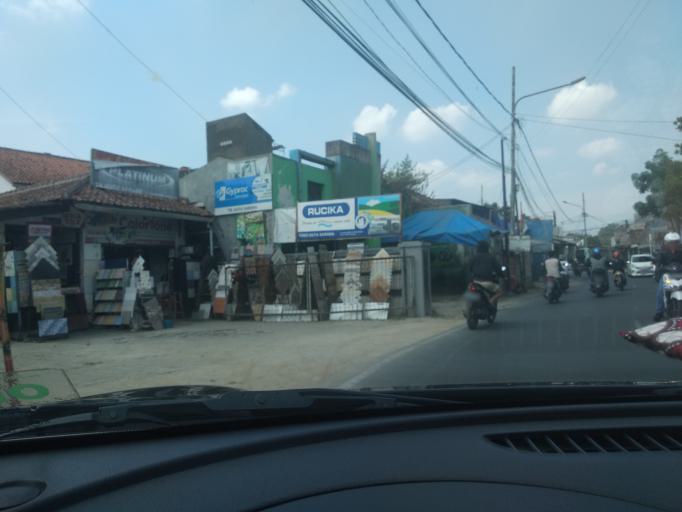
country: ID
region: West Java
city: Cimahi
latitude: -6.8939
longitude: 107.5610
